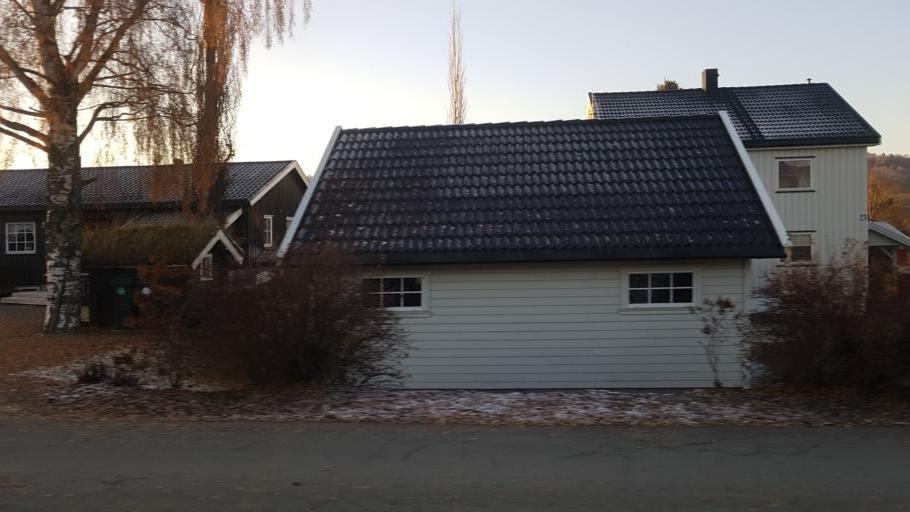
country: NO
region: Sor-Trondelag
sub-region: Melhus
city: Melhus
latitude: 63.3009
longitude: 10.2853
